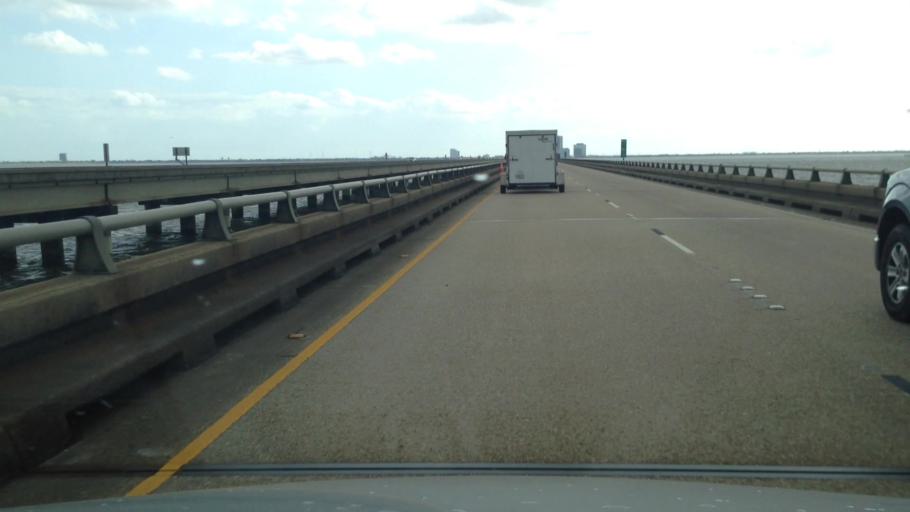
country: US
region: Louisiana
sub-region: Jefferson Parish
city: Metairie
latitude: 30.0640
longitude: -90.1467
